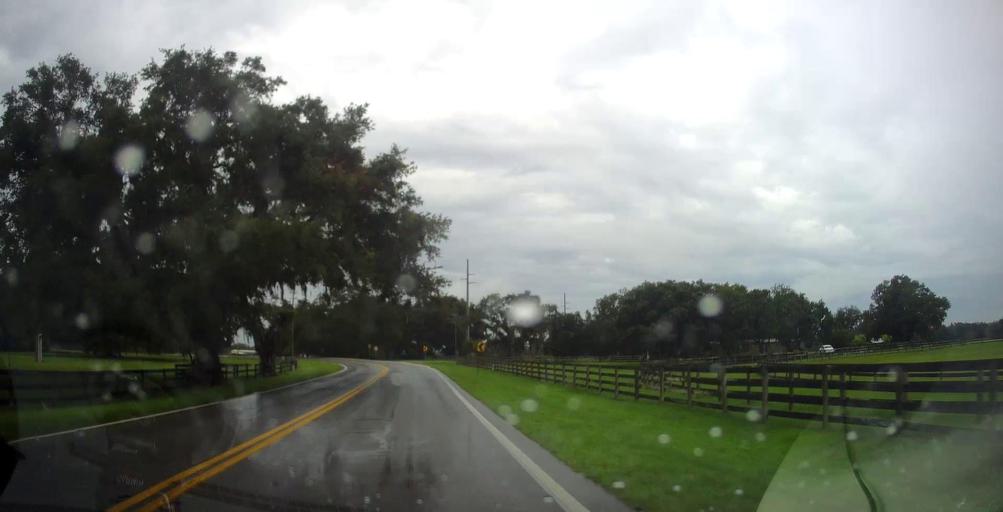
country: US
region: Florida
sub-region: Marion County
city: Citra
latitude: 29.3317
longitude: -82.2062
